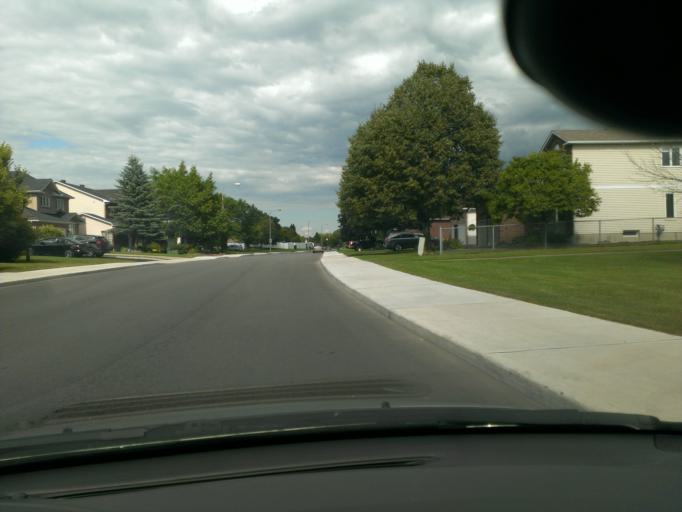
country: CA
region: Quebec
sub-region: Outaouais
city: Gatineau
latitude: 45.4831
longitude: -75.4947
